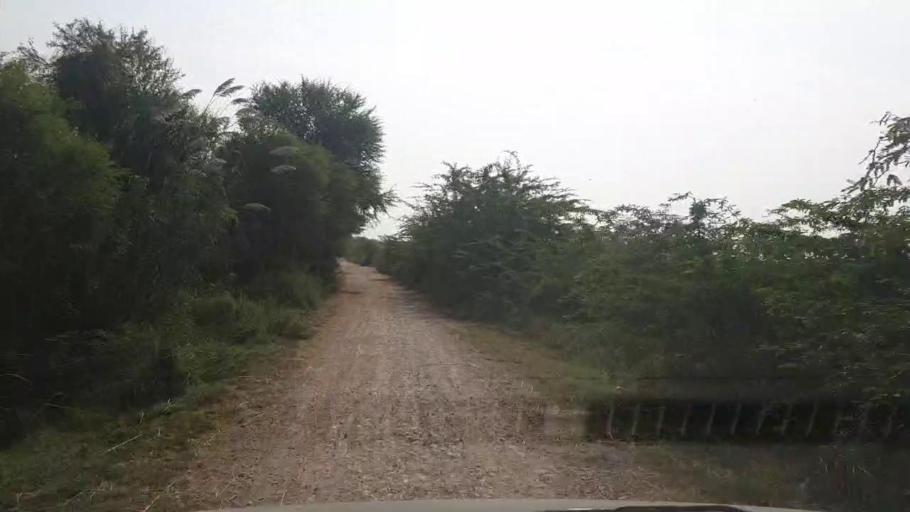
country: PK
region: Sindh
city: Tando Muhammad Khan
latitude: 25.1199
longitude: 68.4390
